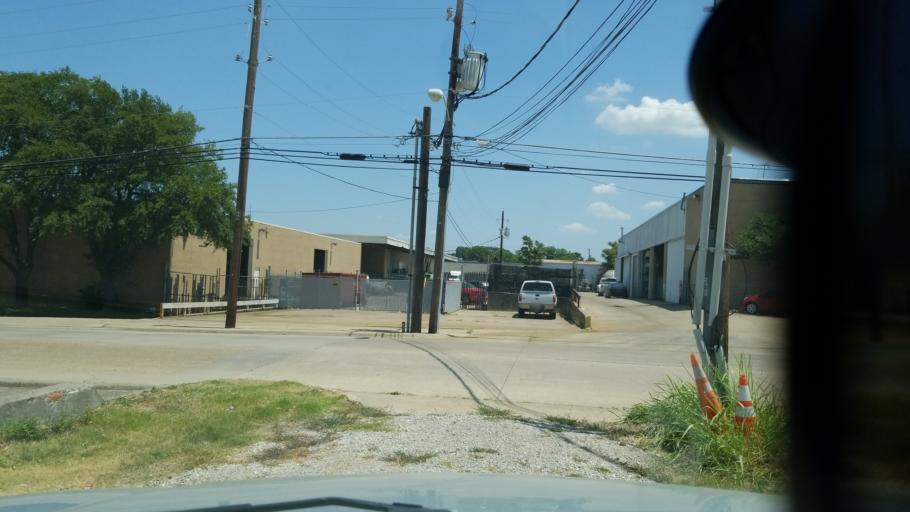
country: US
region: Texas
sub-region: Dallas County
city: Farmers Branch
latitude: 32.8995
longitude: -96.8839
